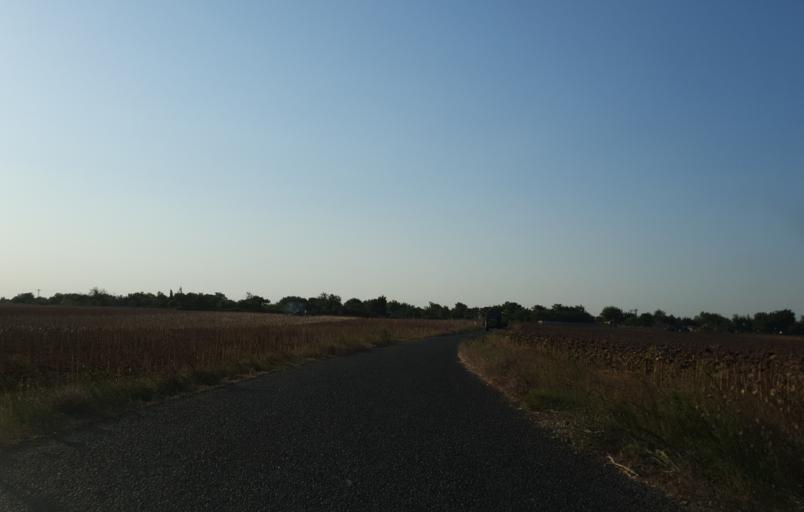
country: TR
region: Tekirdag
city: Beyazkoy
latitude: 41.4299
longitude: 27.7574
